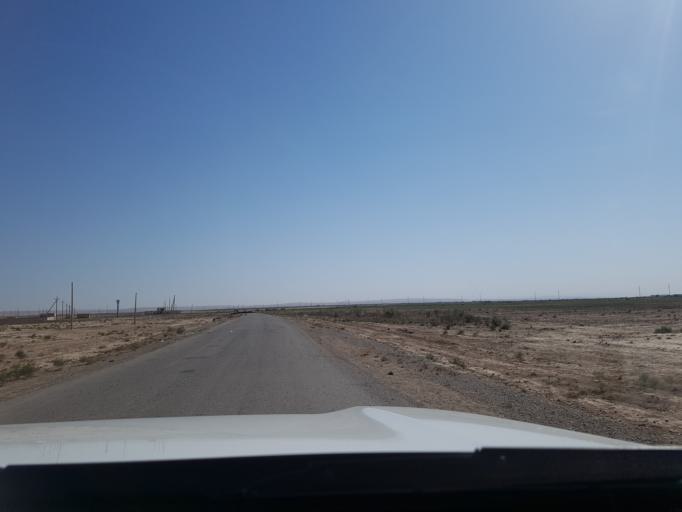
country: IR
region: Razavi Khorasan
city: Sarakhs
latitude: 36.4969
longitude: 61.2537
